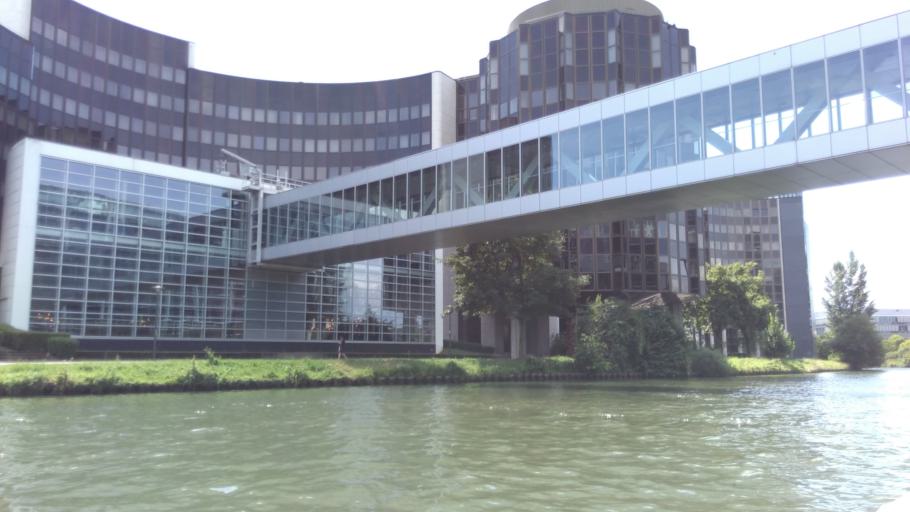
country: FR
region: Alsace
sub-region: Departement du Bas-Rhin
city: Schiltigheim
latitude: 48.5964
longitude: 7.7697
